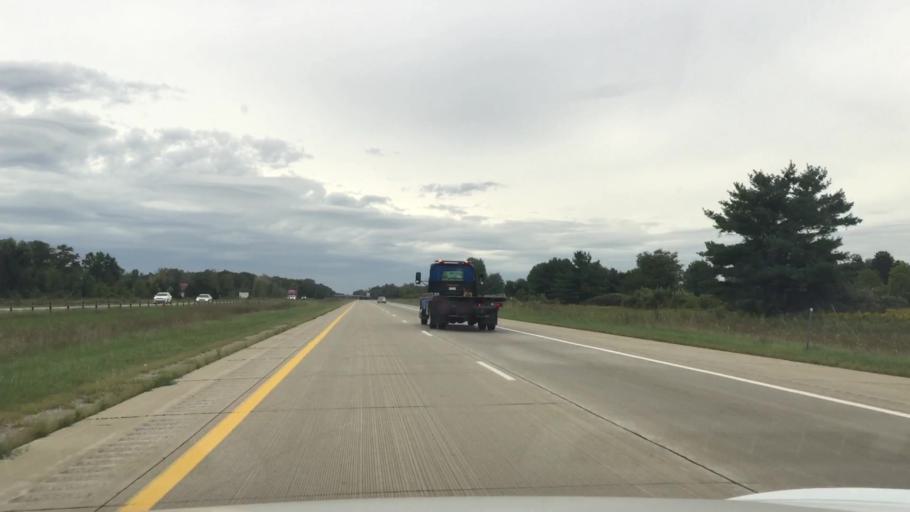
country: US
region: Michigan
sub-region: Saint Clair County
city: Saint Clair
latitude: 42.8473
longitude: -82.5793
